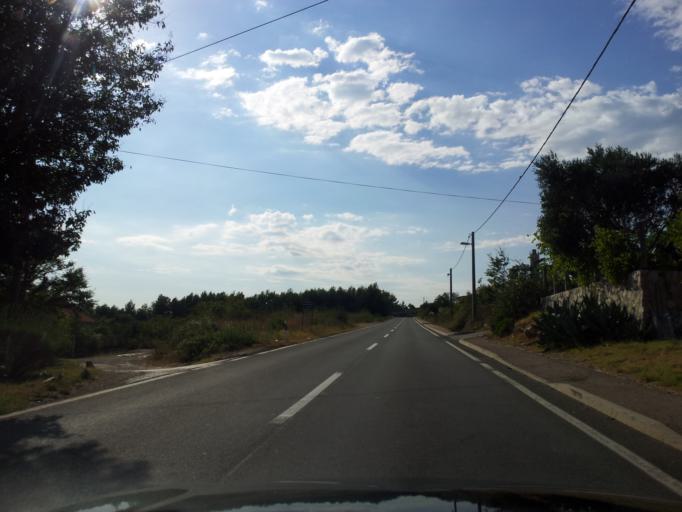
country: HR
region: Zadarska
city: Posedarje
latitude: 44.2172
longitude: 15.4651
